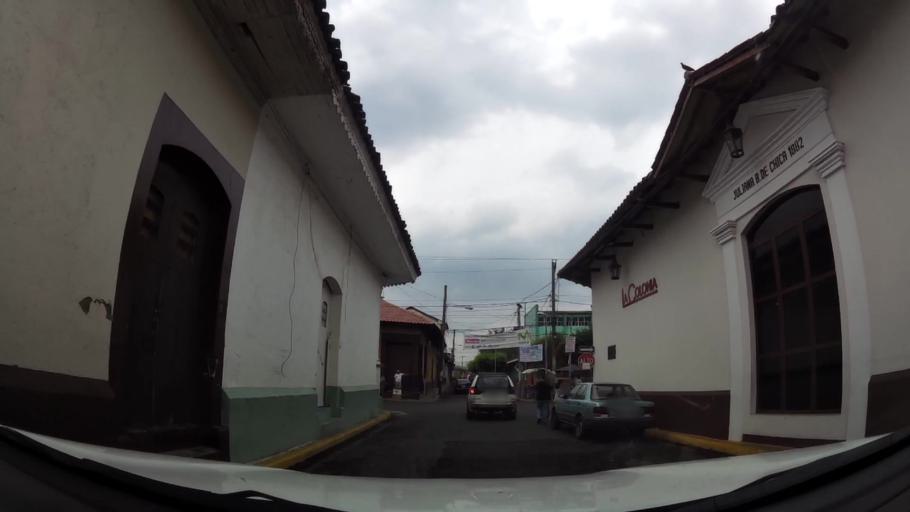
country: NI
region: Leon
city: Leon
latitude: 12.4363
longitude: -86.8830
